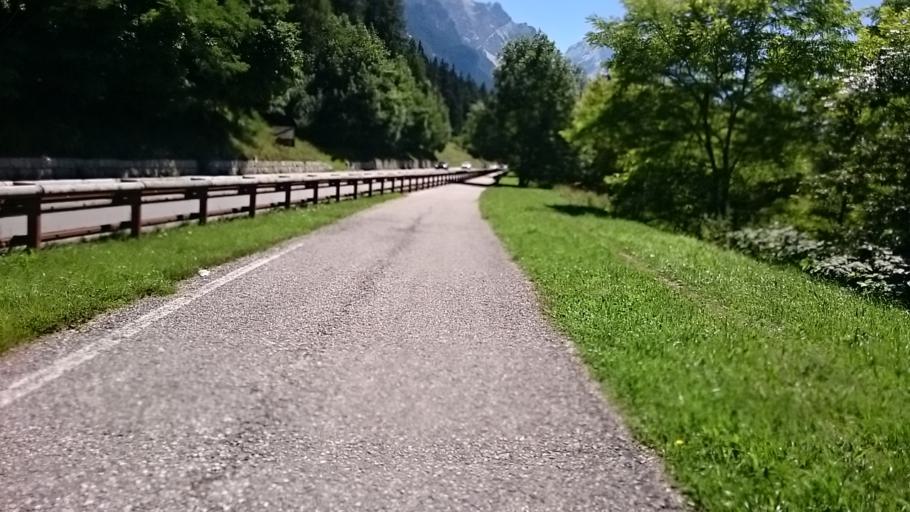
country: IT
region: Veneto
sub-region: Provincia di Belluno
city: Cortina d'Ampezzo
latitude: 46.5136
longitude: 12.1490
